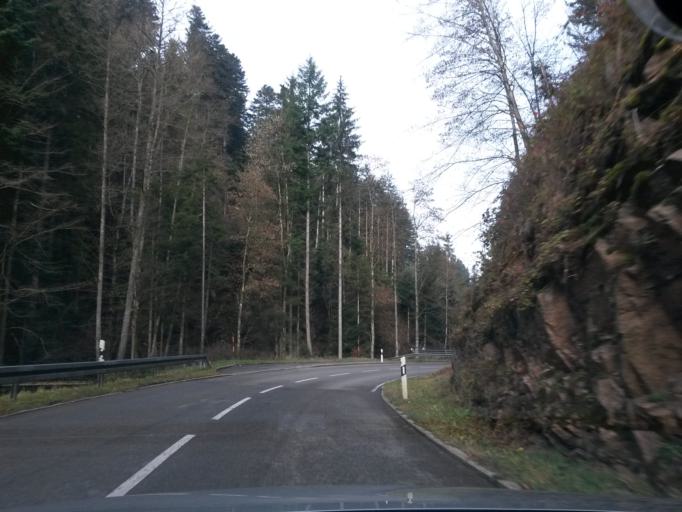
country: DE
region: Baden-Wuerttemberg
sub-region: Freiburg Region
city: Schramberg
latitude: 48.1981
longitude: 8.3831
